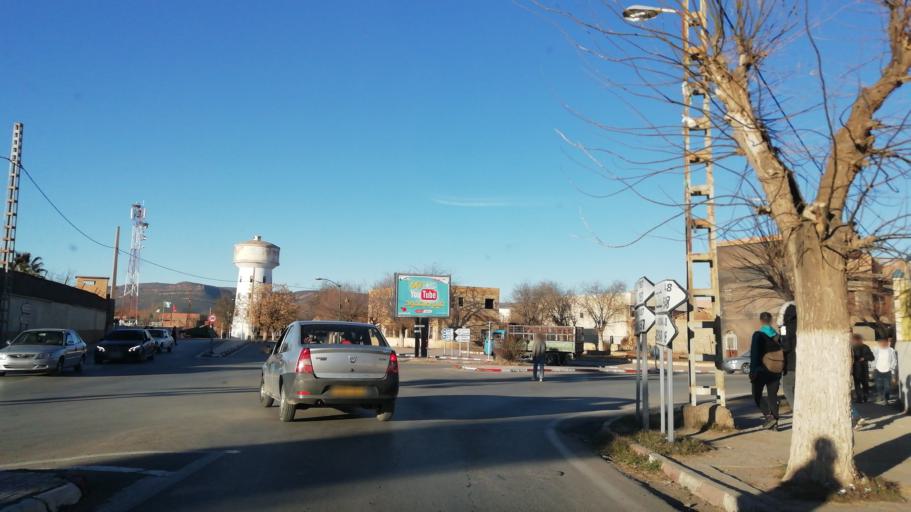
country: DZ
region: Tlemcen
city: Sebdou
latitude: 34.6375
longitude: -1.3329
